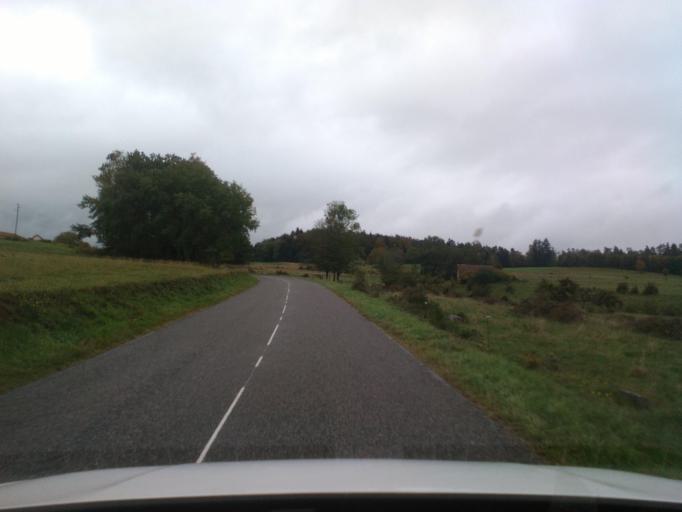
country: FR
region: Lorraine
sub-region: Departement des Vosges
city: Senones
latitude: 48.3640
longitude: 6.9690
